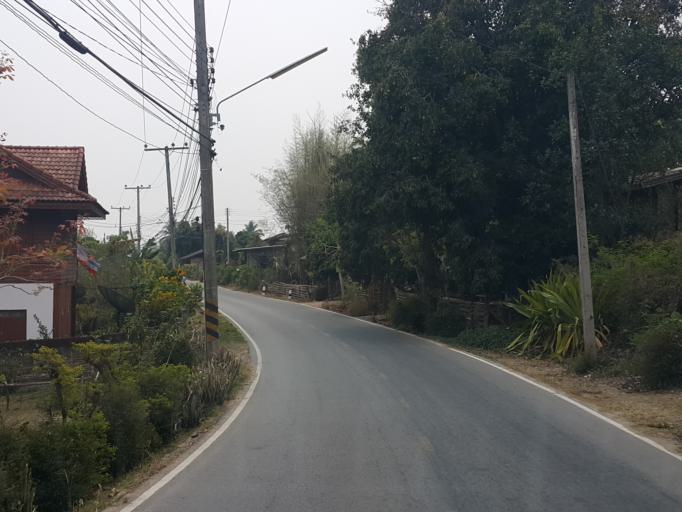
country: TH
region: Chiang Mai
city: Mae Taeng
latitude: 19.0379
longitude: 98.8715
